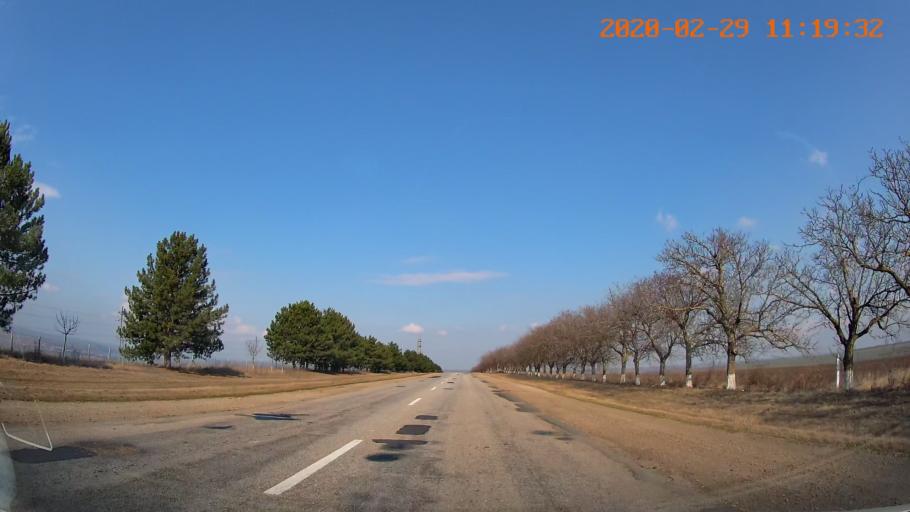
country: MD
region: Telenesti
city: Cocieri
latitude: 47.3514
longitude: 29.1744
